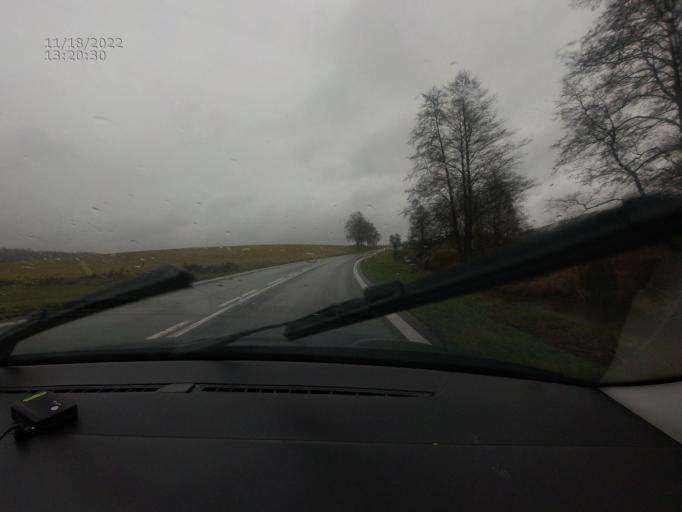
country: CZ
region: Plzensky
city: Horazd'ovice
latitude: 49.3280
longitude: 13.6733
